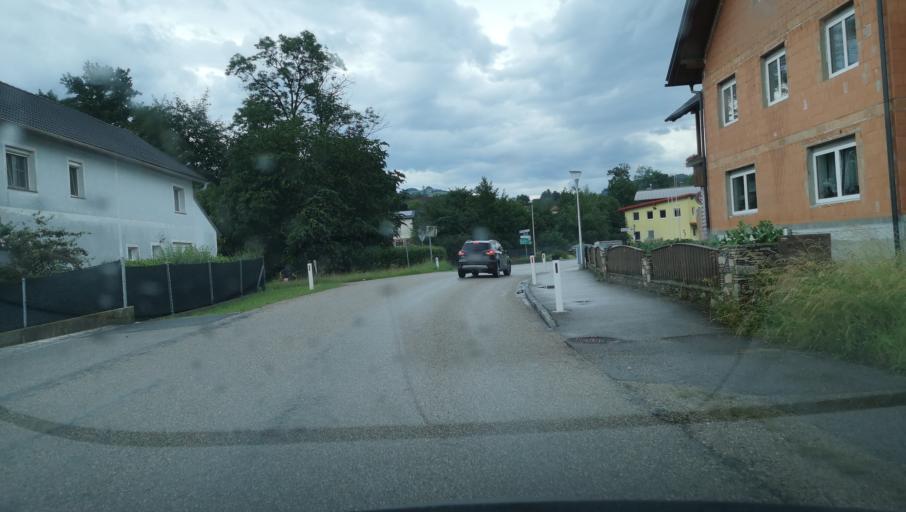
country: AT
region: Lower Austria
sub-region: Politischer Bezirk Amstetten
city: Neuhofen an der Ybbs
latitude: 48.0299
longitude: 14.8370
